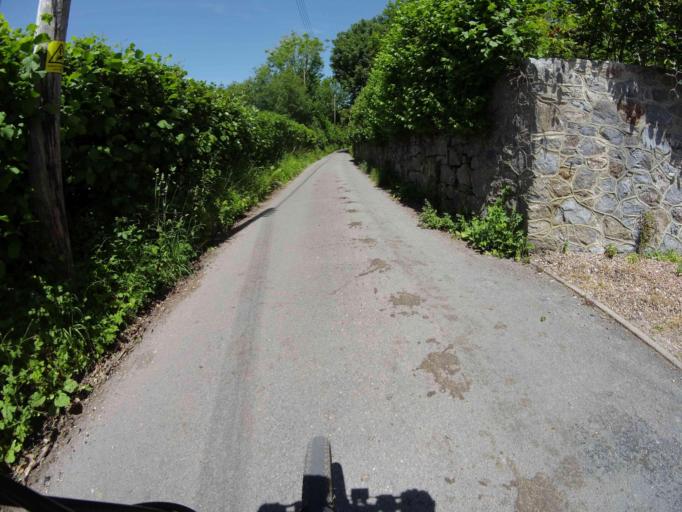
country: GB
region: England
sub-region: Devon
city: Bovey Tracey
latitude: 50.6185
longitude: -3.7139
